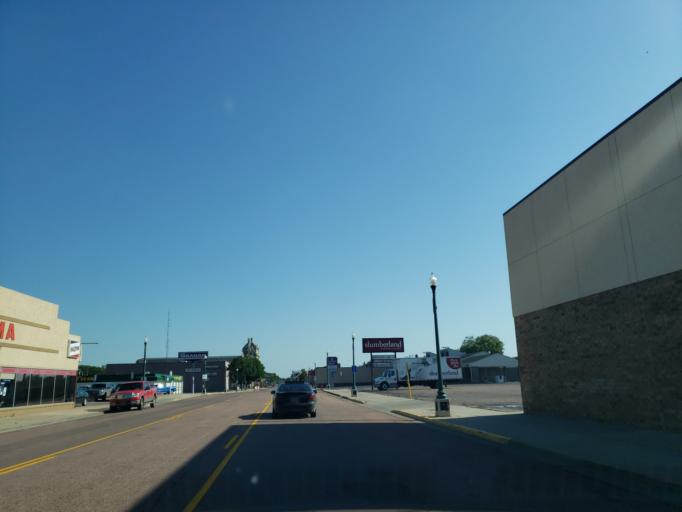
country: US
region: South Dakota
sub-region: Davison County
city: Mitchell
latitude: 43.7174
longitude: -98.0256
